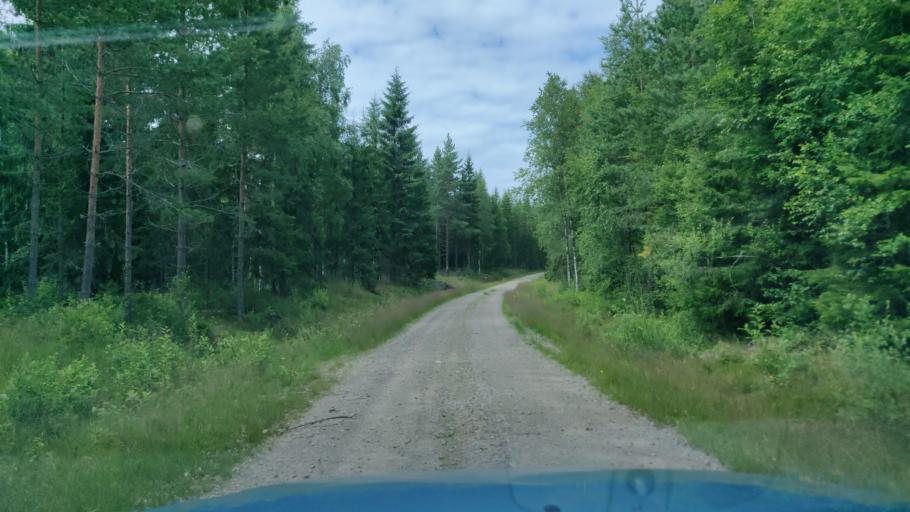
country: SE
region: Vaermland
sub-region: Hagfors Kommun
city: Hagfors
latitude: 59.9414
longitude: 13.5970
